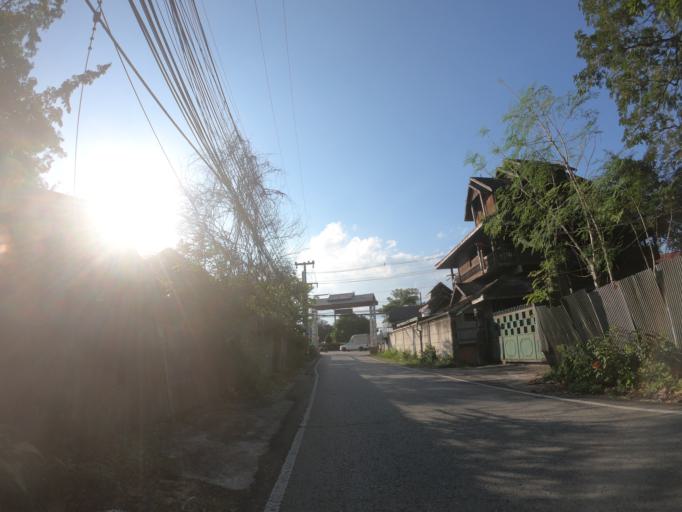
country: TH
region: Chiang Mai
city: Chiang Mai
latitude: 18.7542
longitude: 98.9677
